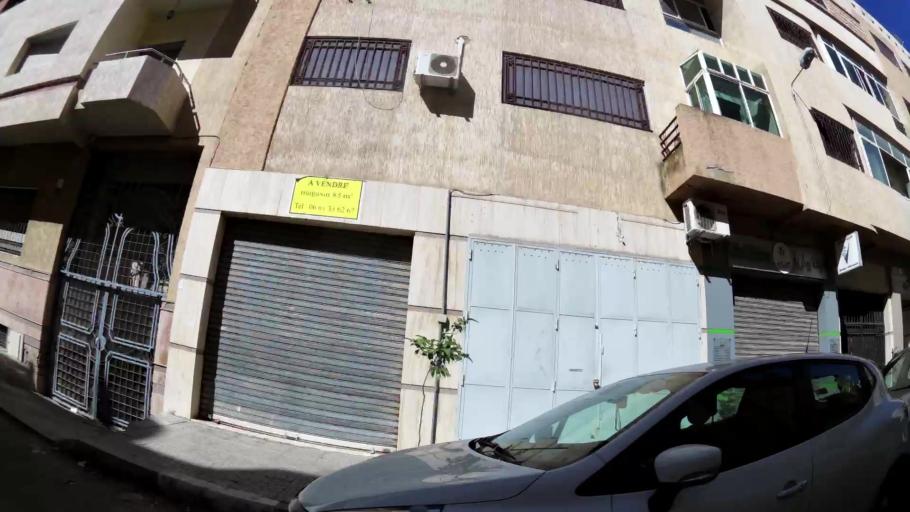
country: MA
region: Fes-Boulemane
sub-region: Fes
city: Fes
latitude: 34.0264
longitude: -4.9932
